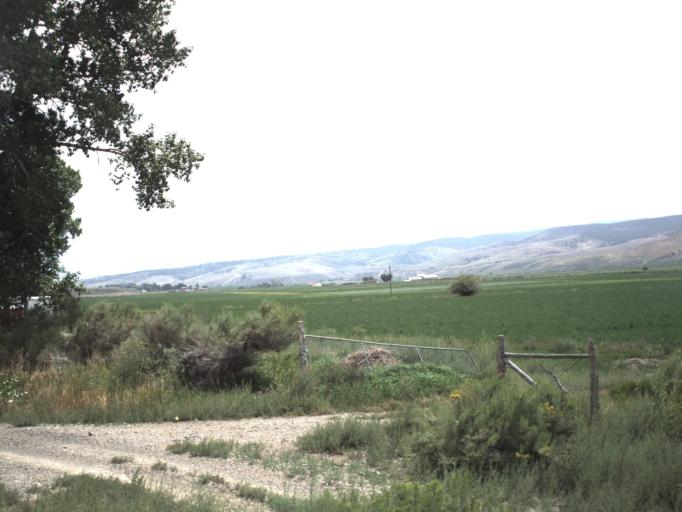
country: US
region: Utah
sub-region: Piute County
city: Junction
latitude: 38.1490
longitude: -112.0005
